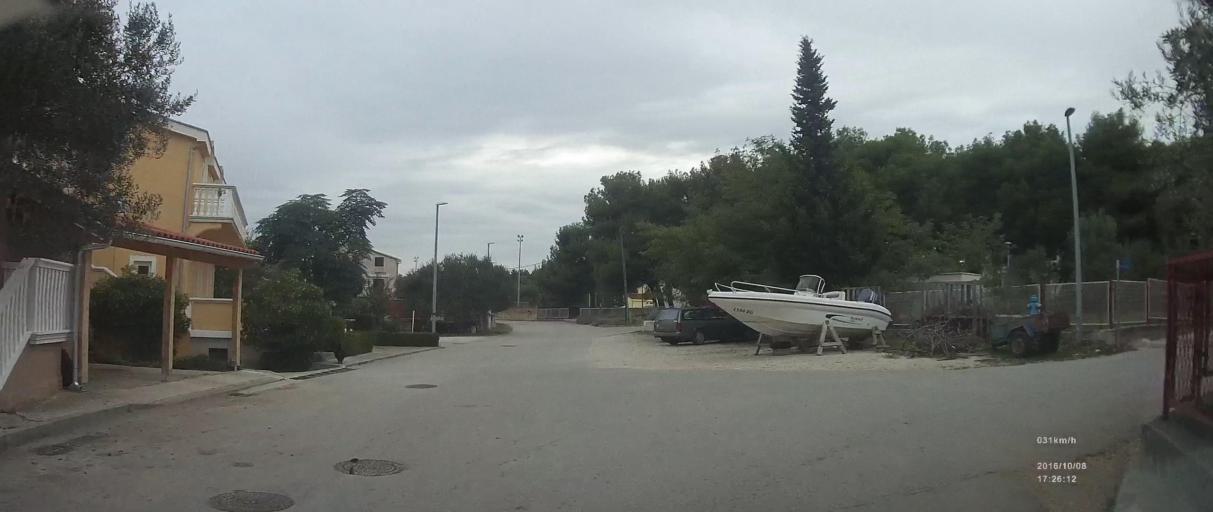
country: HR
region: Zadarska
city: Pakostane
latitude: 43.9127
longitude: 15.5023
